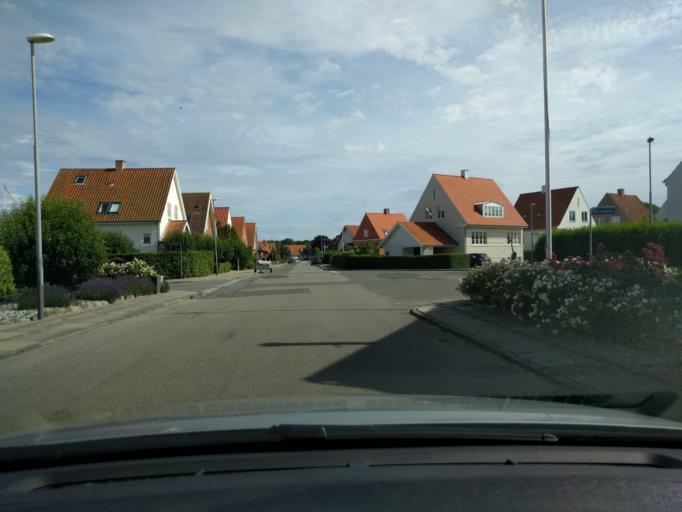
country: DK
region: South Denmark
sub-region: Kerteminde Kommune
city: Kerteminde
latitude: 55.4483
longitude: 10.6635
